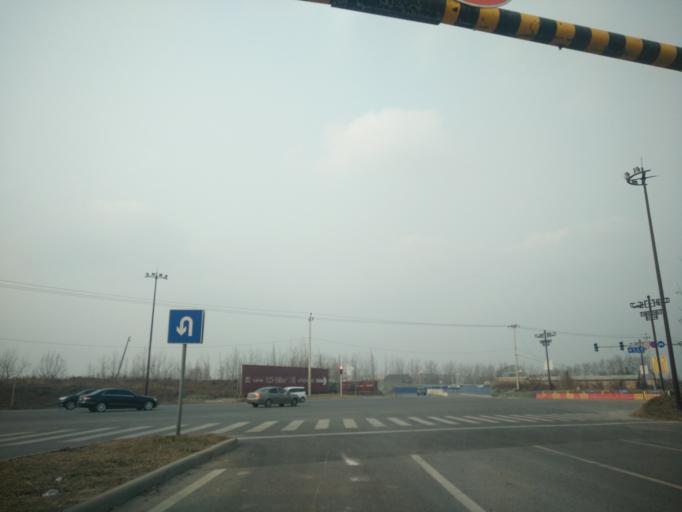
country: CN
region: Beijing
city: Yinghai
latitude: 39.7747
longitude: 116.4421
